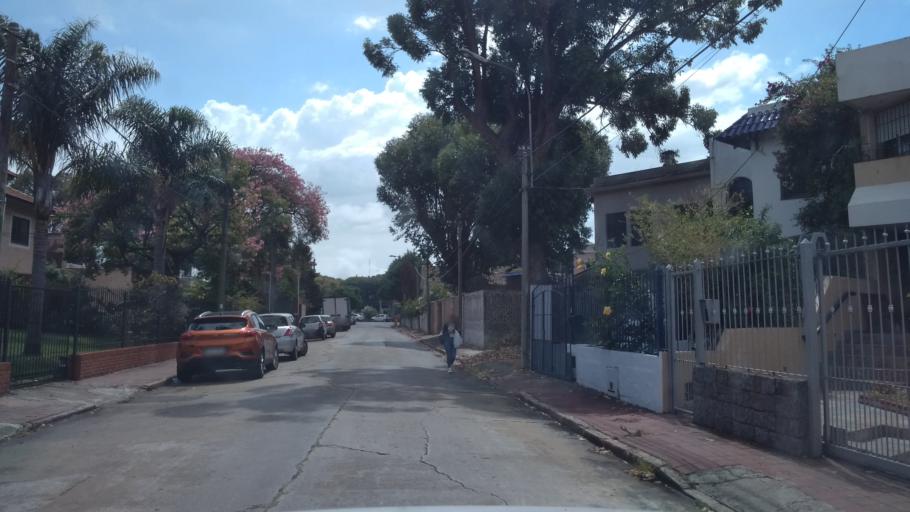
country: UY
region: Canelones
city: Paso de Carrasco
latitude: -34.8944
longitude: -56.0660
